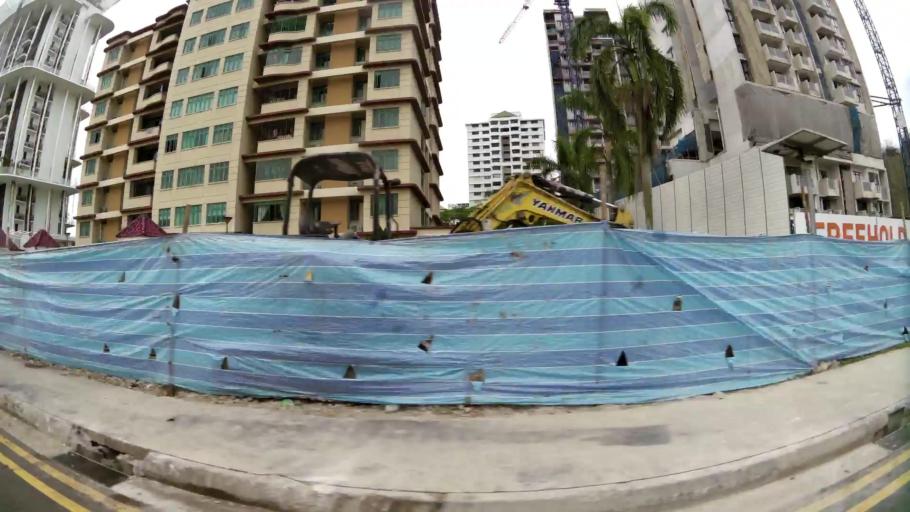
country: SG
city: Singapore
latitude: 1.3614
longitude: 103.8912
